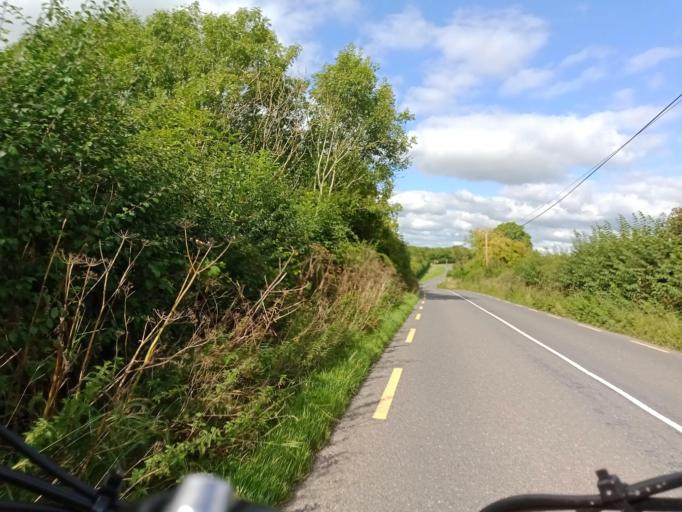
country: IE
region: Leinster
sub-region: Kilkenny
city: Kilkenny
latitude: 52.5869
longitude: -7.2685
